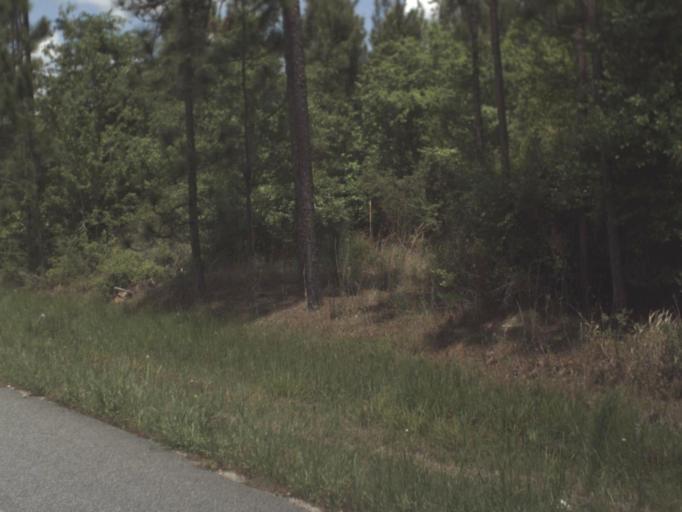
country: US
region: Alabama
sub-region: Escambia County
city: Atmore
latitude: 30.8578
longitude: -87.4423
